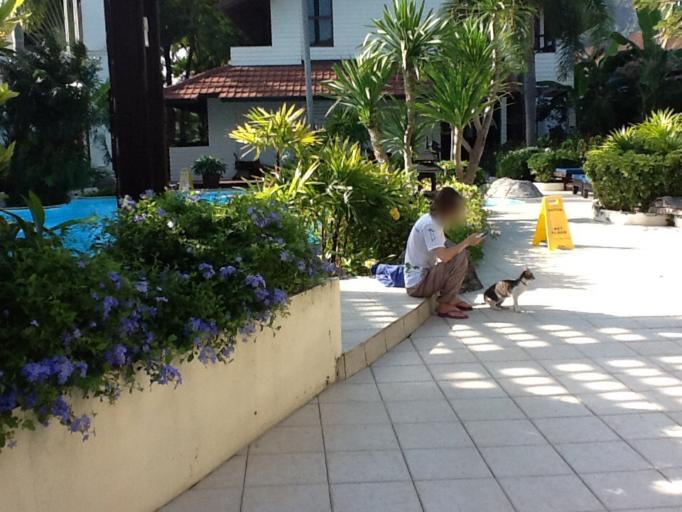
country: TH
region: Phangnga
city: Ban Phru Nai
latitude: 7.7392
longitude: 98.7729
